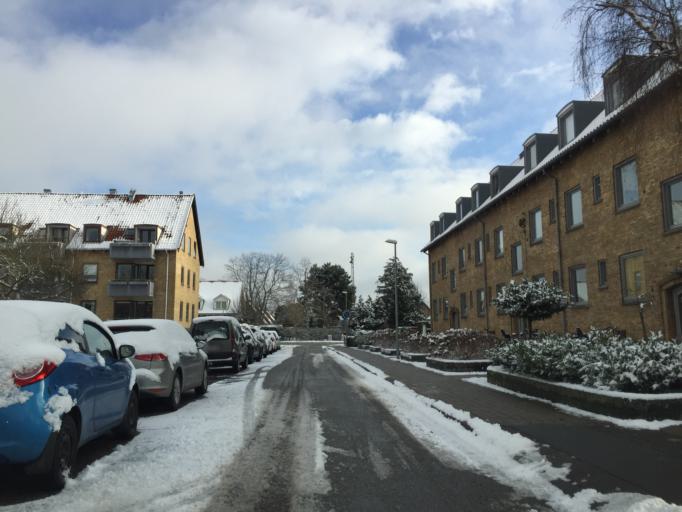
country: DK
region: Capital Region
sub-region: Tarnby Kommune
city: Tarnby
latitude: 55.6329
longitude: 12.6432
